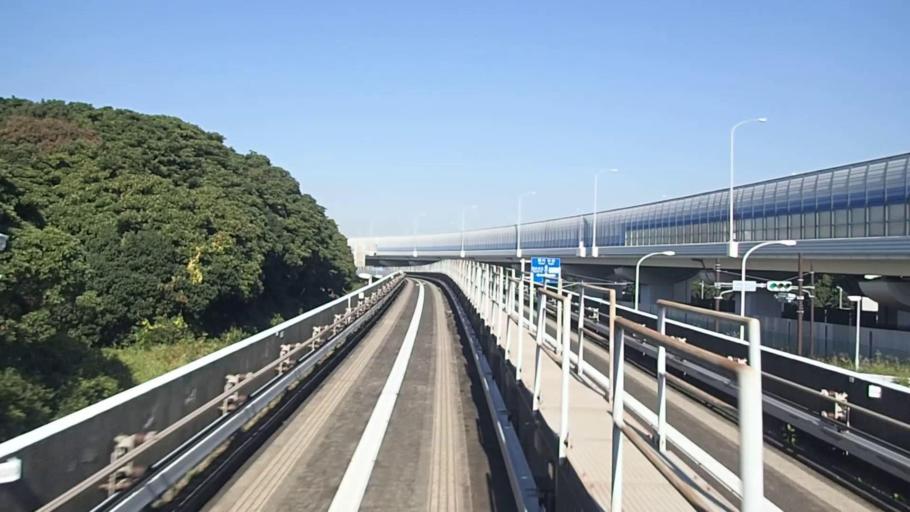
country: JP
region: Kanagawa
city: Yokohama
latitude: 35.3745
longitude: 139.6426
